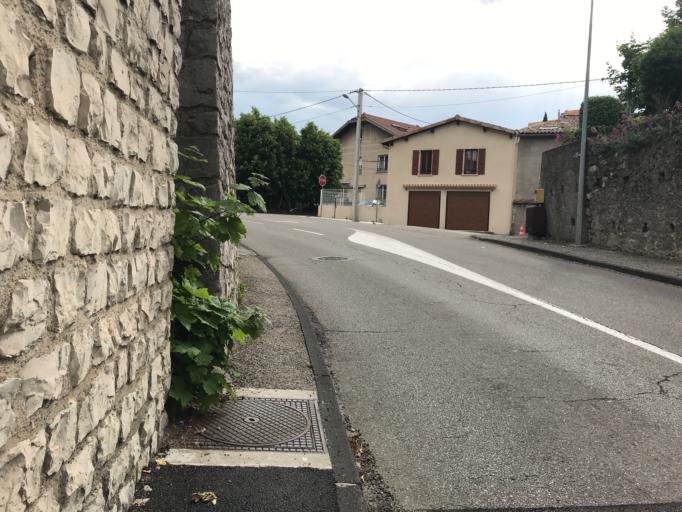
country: FR
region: Rhone-Alpes
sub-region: Departement de l'Ardeche
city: Privas
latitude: 44.7308
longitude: 4.5971
